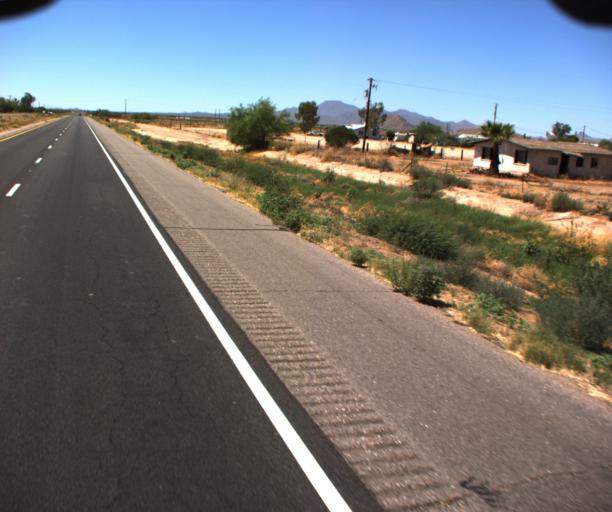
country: US
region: Arizona
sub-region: Pinal County
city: Maricopa
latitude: 32.9053
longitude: -112.0496
